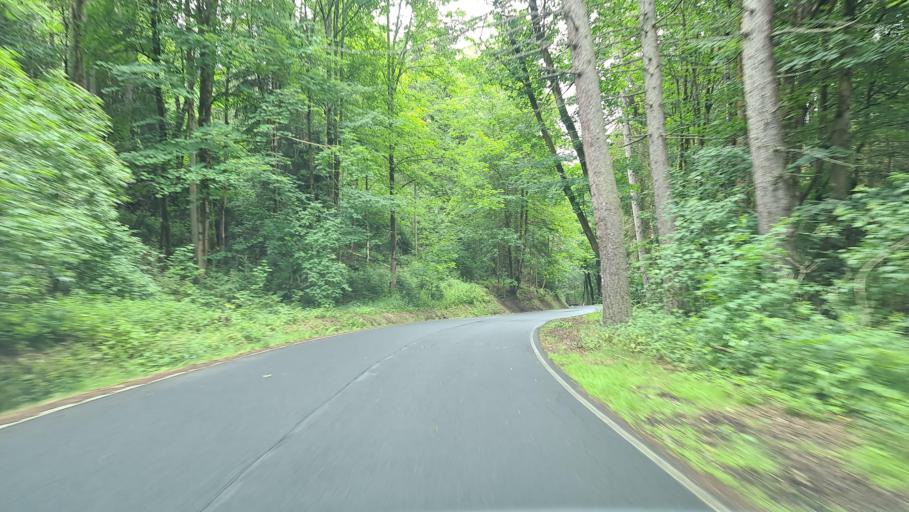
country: CZ
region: Karlovarsky
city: Kraslice
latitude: 50.3765
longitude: 12.5148
